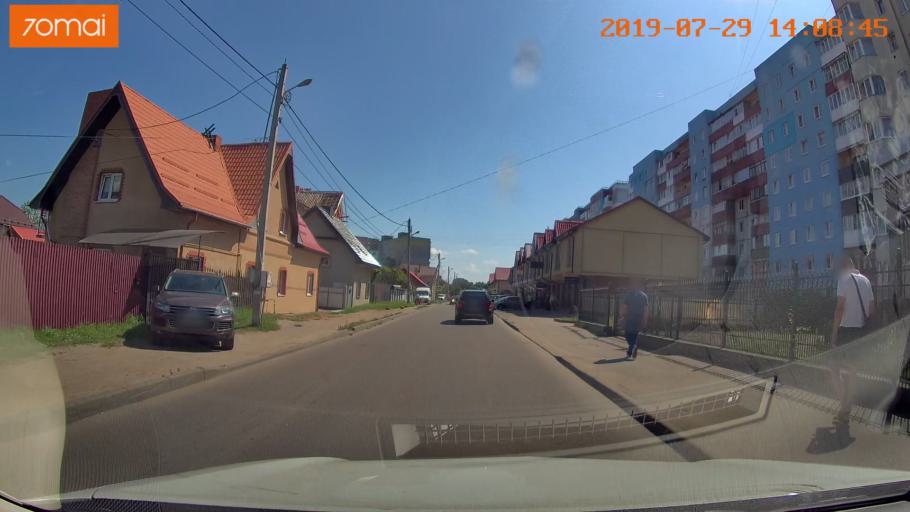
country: RU
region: Kaliningrad
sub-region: Gorod Kaliningrad
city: Baltiysk
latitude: 54.6570
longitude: 19.9073
